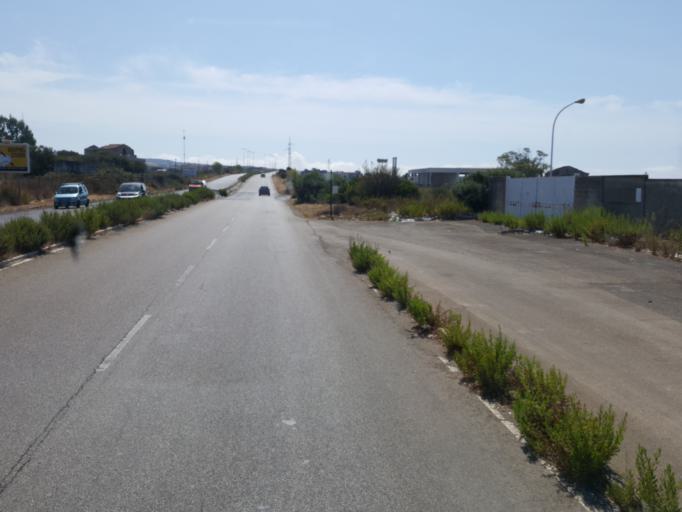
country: IT
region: Latium
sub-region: Citta metropolitana di Roma Capitale
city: Civitavecchia
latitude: 42.1108
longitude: 11.7838
